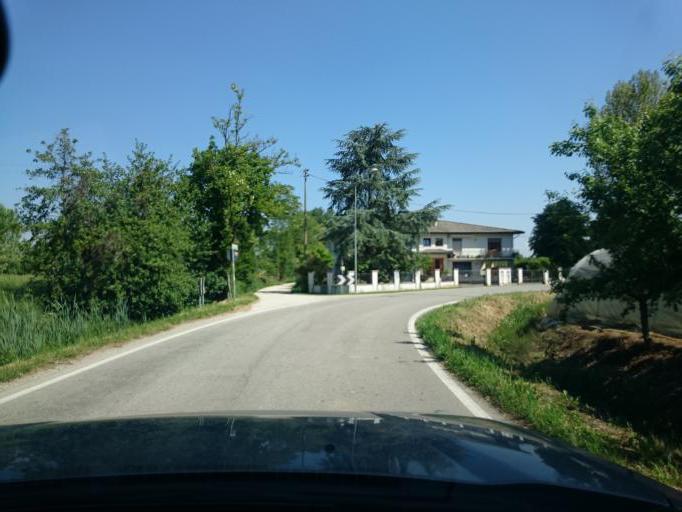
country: IT
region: Veneto
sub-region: Provincia di Venezia
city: Stigliano
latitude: 45.5353
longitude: 12.0514
